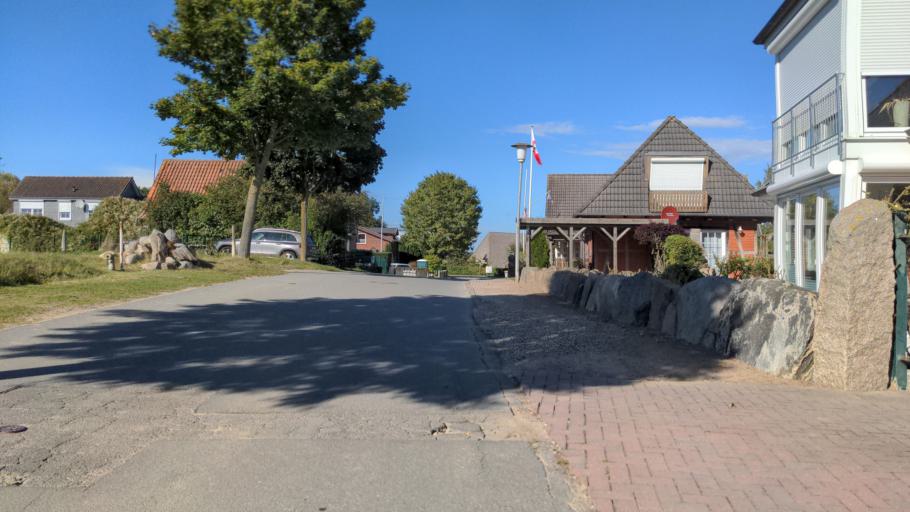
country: DE
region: Schleswig-Holstein
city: Gromitz
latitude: 54.1717
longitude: 10.9392
